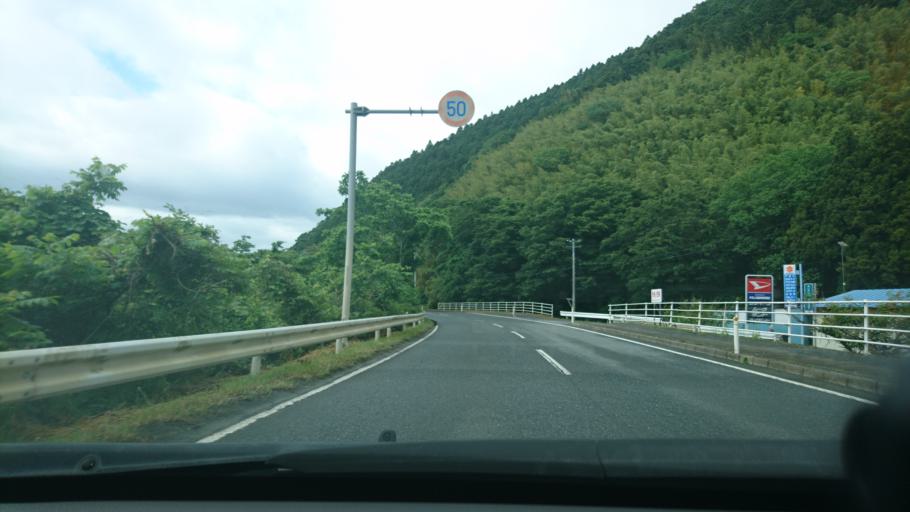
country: JP
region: Miyagi
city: Ishinomaki
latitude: 38.5935
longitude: 141.3049
